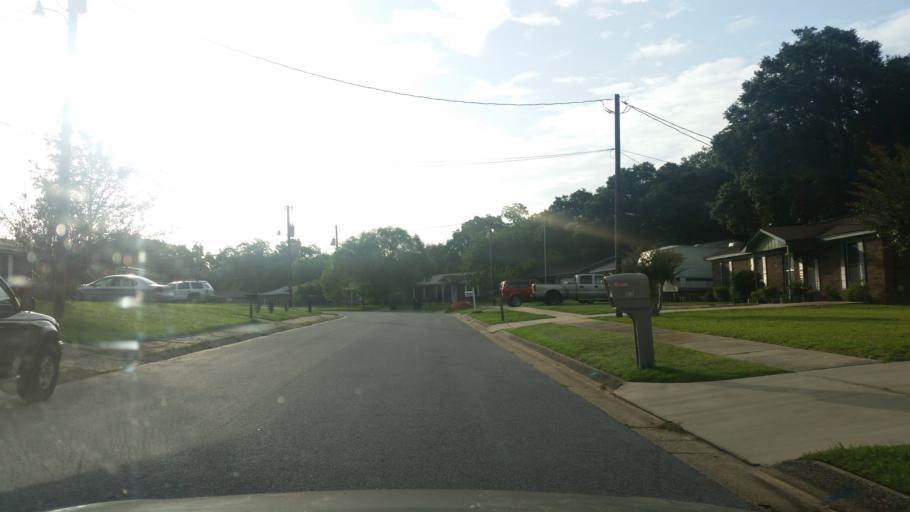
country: US
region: Florida
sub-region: Escambia County
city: Bellview
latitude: 30.4456
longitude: -87.3085
